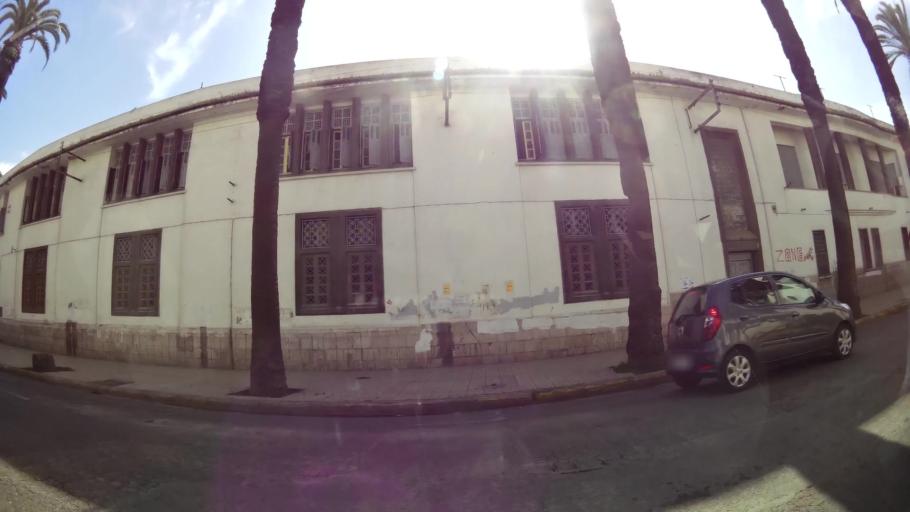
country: MA
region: Grand Casablanca
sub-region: Casablanca
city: Casablanca
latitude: 33.5943
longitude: -7.6238
